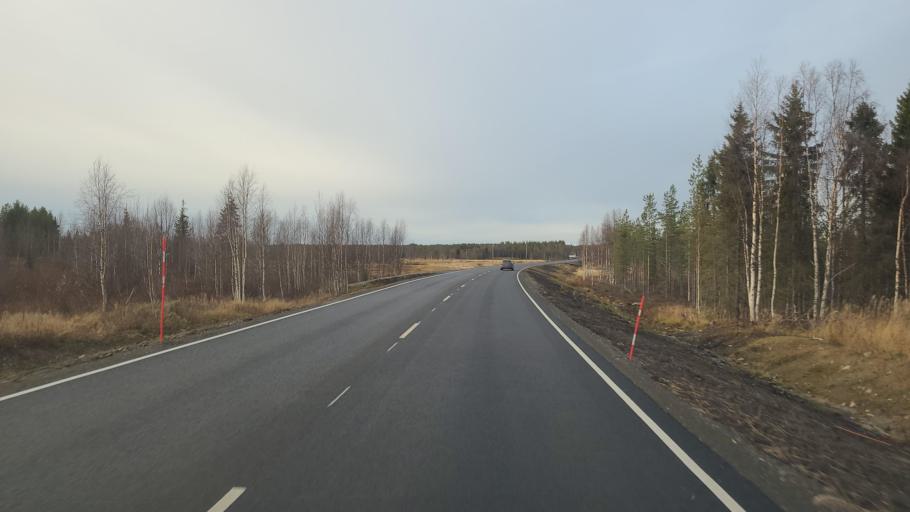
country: FI
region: Lapland
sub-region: Tunturi-Lappi
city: Kittilae
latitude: 67.8732
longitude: 24.8955
